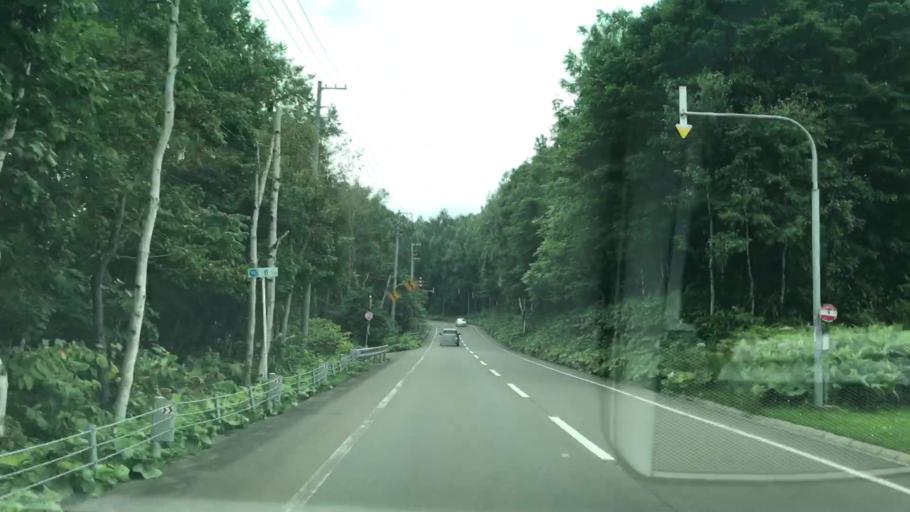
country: JP
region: Hokkaido
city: Yoichi
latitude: 43.1340
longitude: 140.8246
